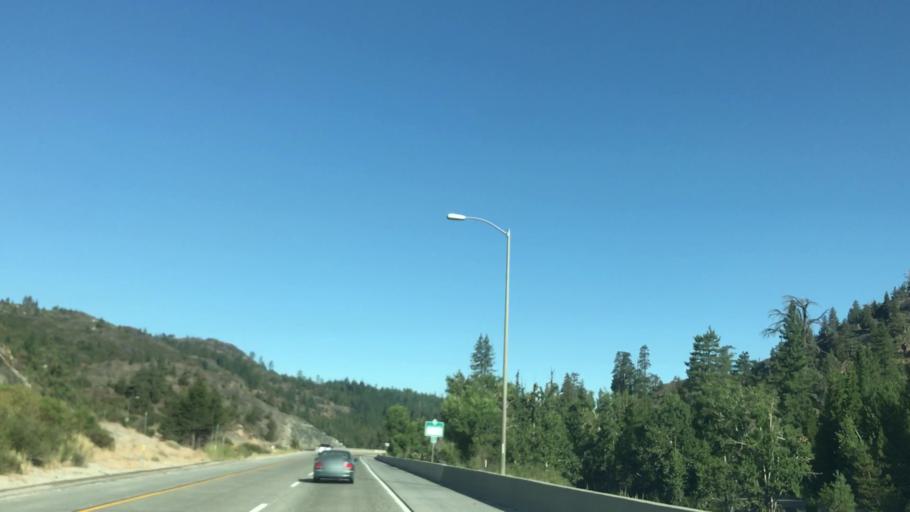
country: US
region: California
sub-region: Sierra County
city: Downieville
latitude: 39.3148
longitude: -120.5530
